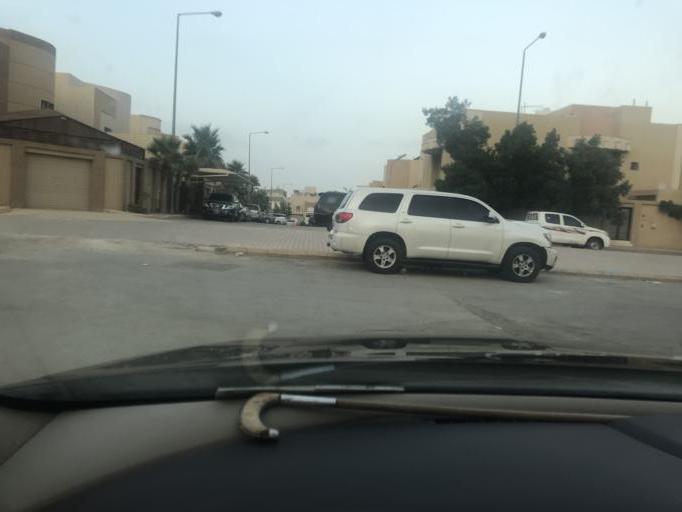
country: SA
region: Ar Riyad
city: Riyadh
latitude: 24.7309
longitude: 46.7462
